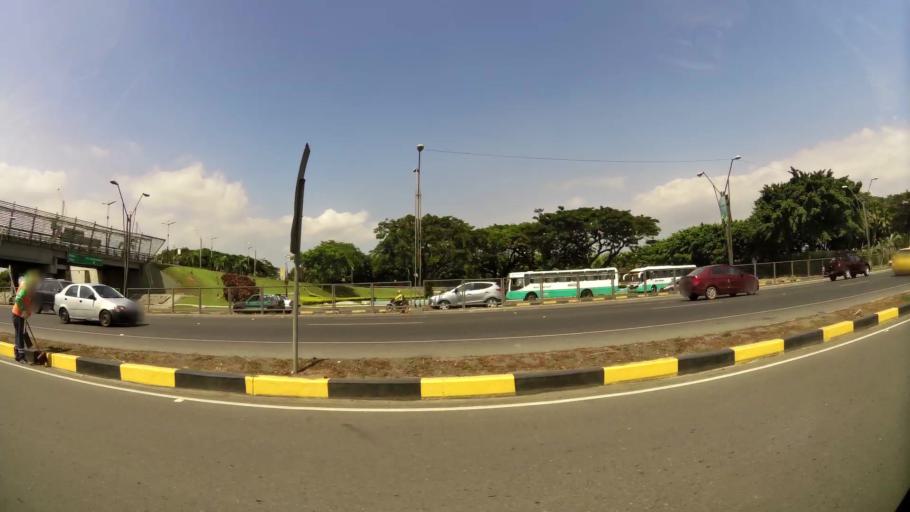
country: EC
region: Guayas
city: Eloy Alfaro
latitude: -2.1523
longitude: -79.8660
